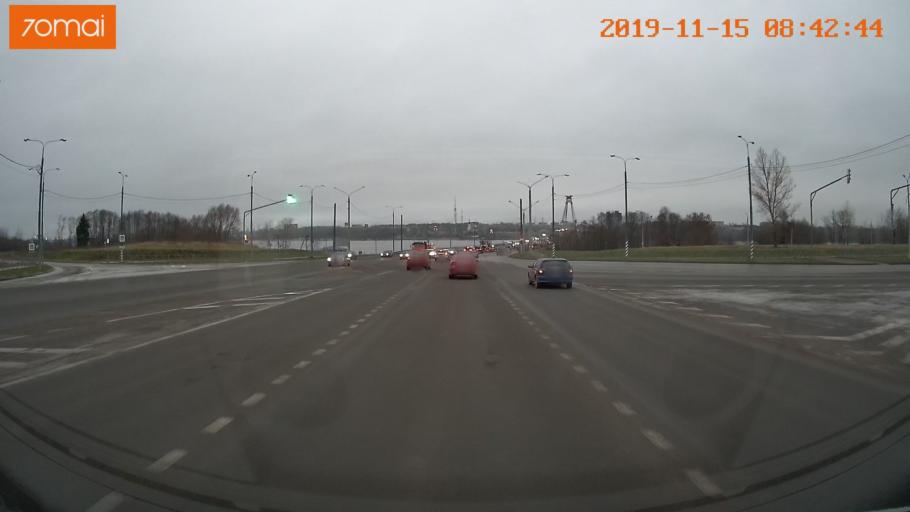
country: RU
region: Vologda
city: Cherepovets
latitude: 59.1050
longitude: 37.9066
